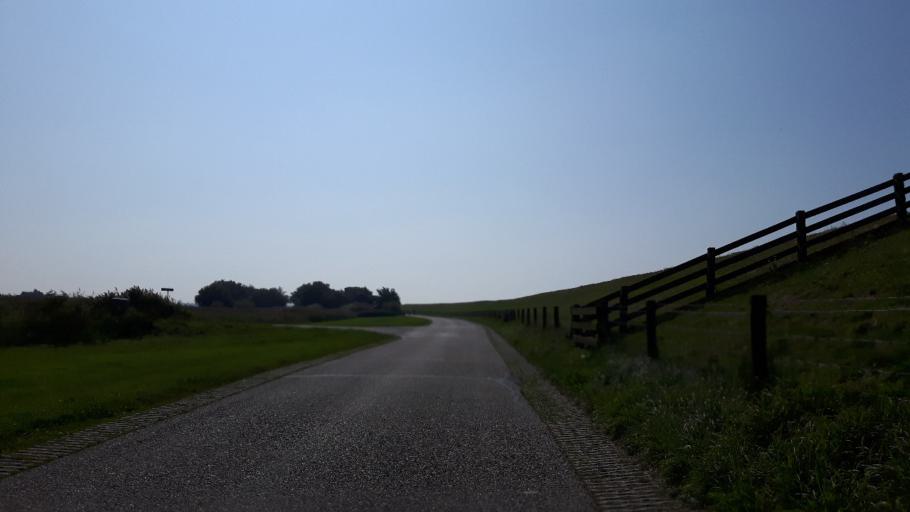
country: NL
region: Friesland
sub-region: Sudwest Fryslan
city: Makkum
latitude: 53.0861
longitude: 5.3827
